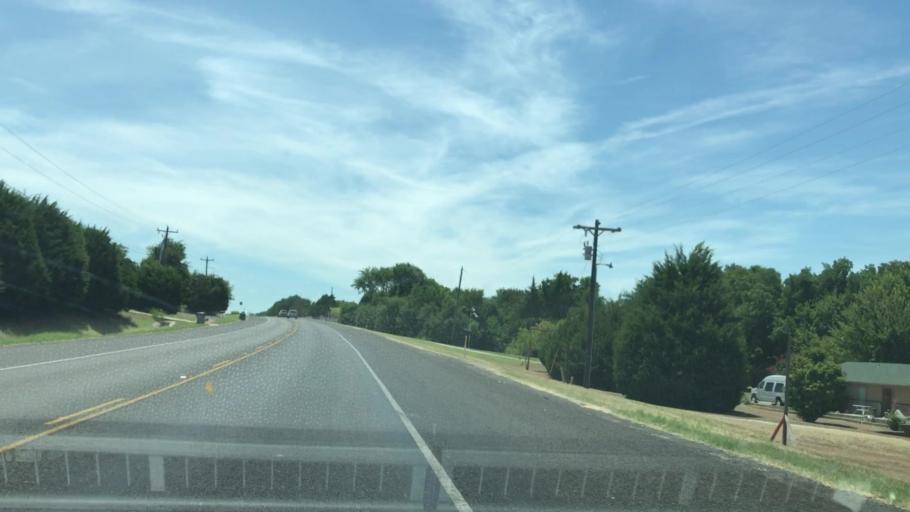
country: US
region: Texas
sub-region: Collin County
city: Lavon
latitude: 32.9979
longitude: -96.4655
